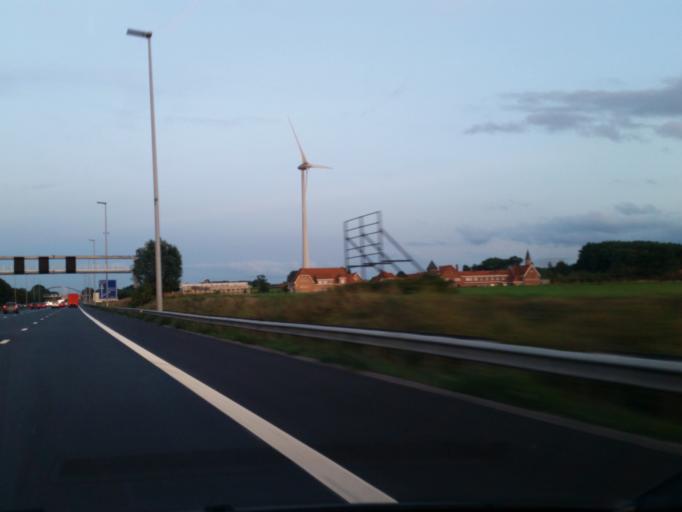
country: BE
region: Flanders
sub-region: Provincie Oost-Vlaanderen
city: Melle
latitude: 50.9828
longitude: 3.8171
